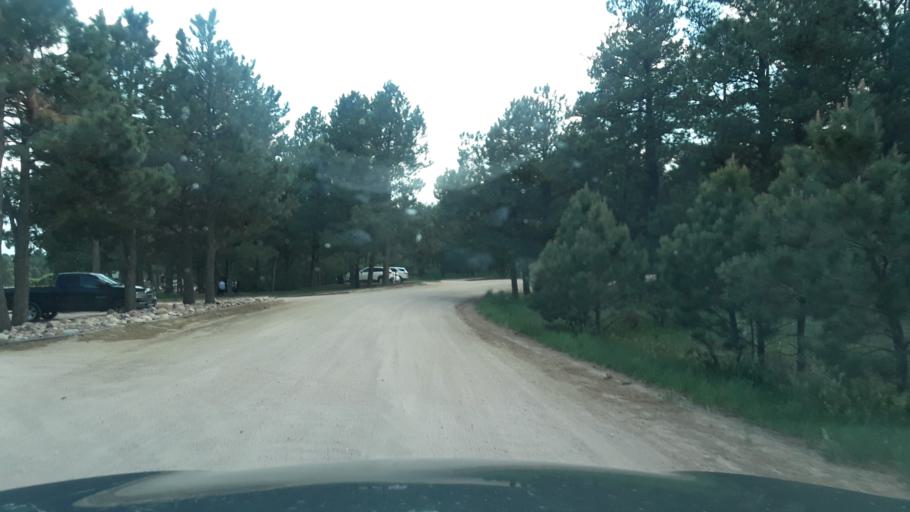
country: US
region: Colorado
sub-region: El Paso County
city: Gleneagle
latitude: 39.0597
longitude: -104.7875
